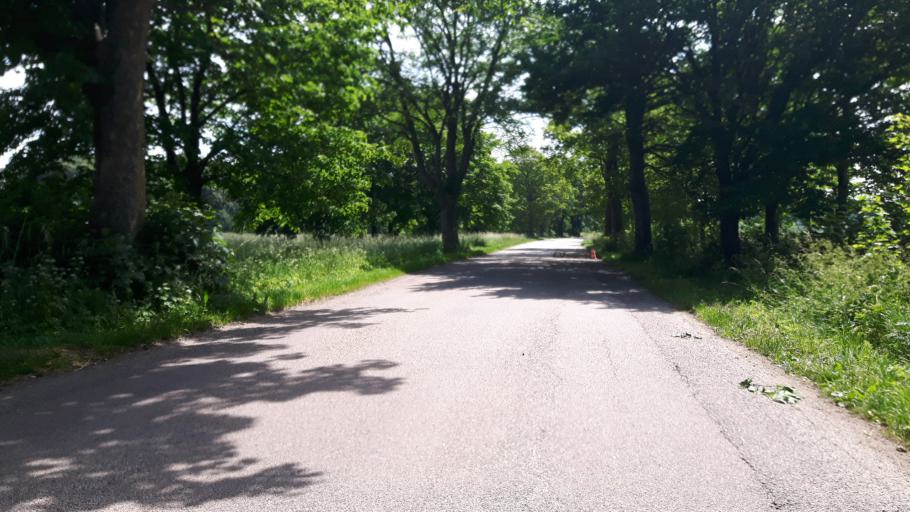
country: PL
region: Pomeranian Voivodeship
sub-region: Powiat wejherowski
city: Choczewo
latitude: 54.7424
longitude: 17.8127
